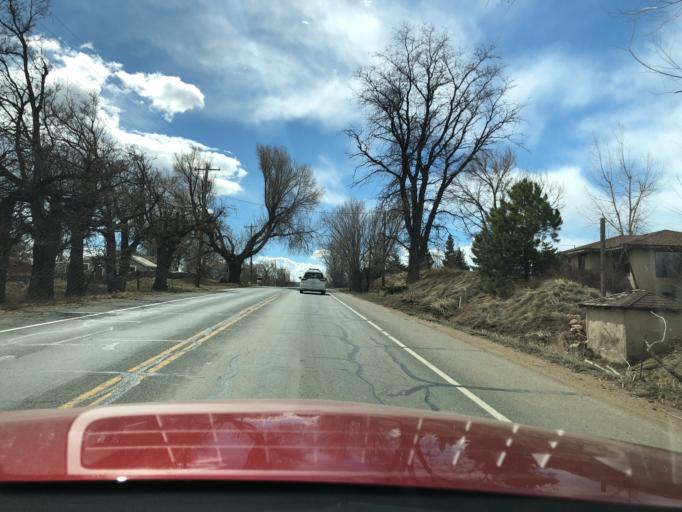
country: US
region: Colorado
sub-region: Boulder County
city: Gunbarrel
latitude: 40.0301
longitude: -105.1785
